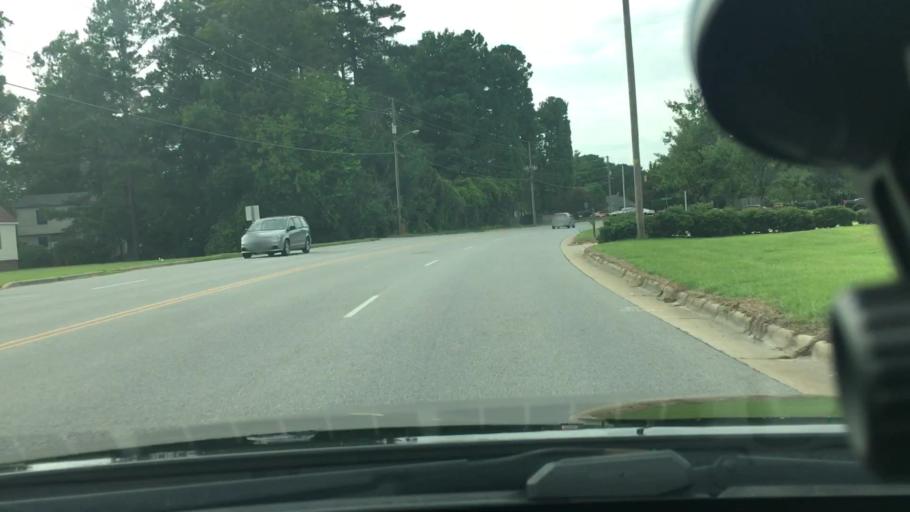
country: US
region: North Carolina
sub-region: Pitt County
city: Greenville
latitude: 35.5852
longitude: -77.3462
